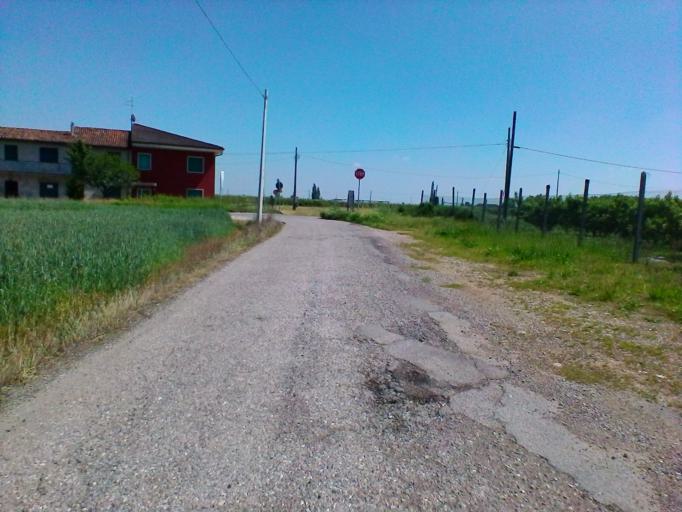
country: IT
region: Veneto
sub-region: Provincia di Verona
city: Alpo
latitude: 45.3690
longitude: 10.8958
